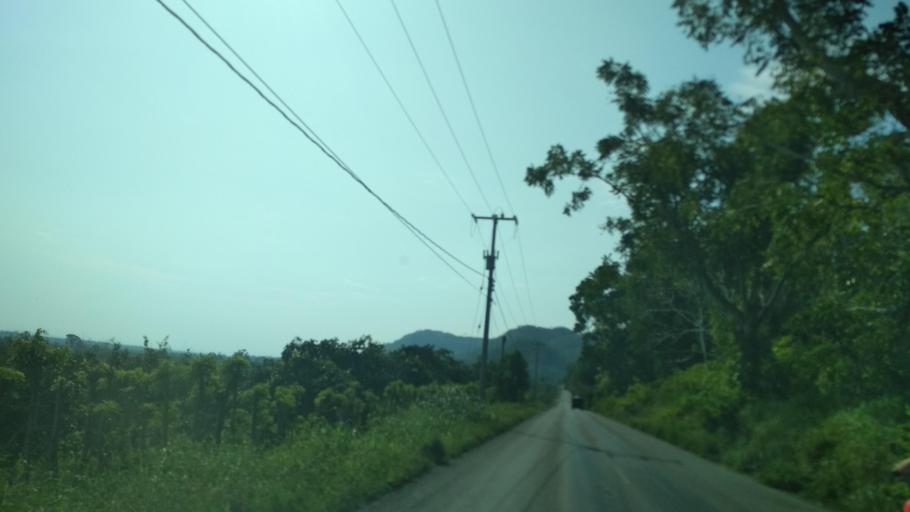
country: MX
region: Veracruz
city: Agua Dulce
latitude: 20.3995
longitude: -97.2543
